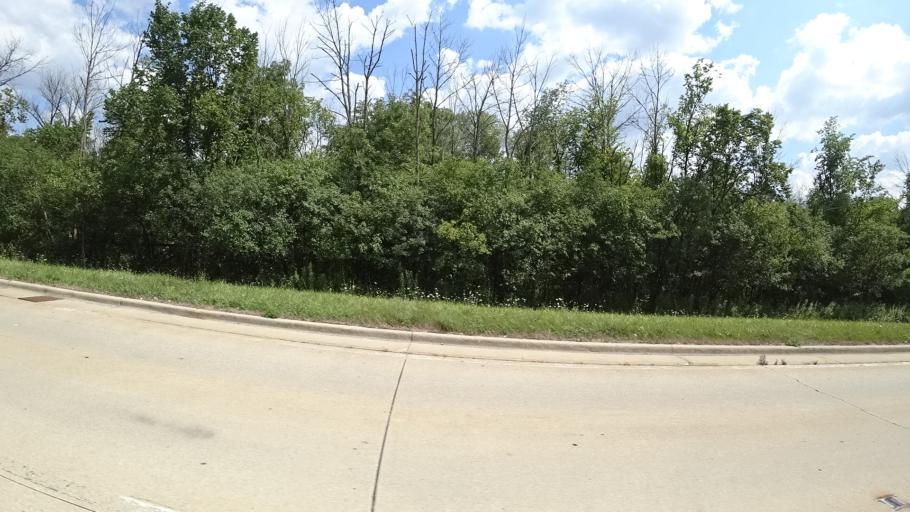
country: US
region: Illinois
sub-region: Cook County
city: Crestwood
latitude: 41.6382
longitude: -87.7767
